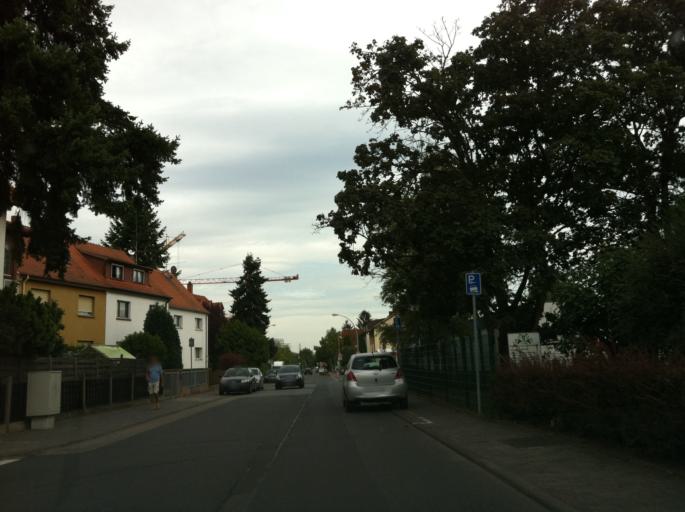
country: DE
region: Hesse
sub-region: Regierungsbezirk Darmstadt
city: Bad Soden am Taunus
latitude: 50.1403
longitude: 8.5081
